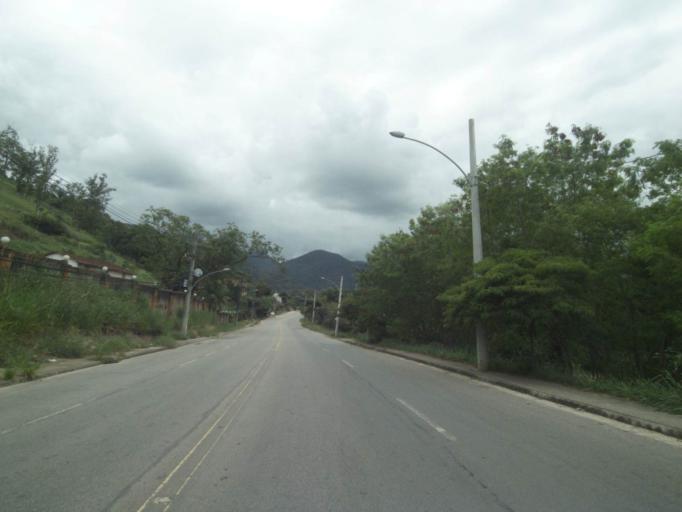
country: BR
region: Rio de Janeiro
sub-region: Nilopolis
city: Nilopolis
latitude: -22.9904
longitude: -43.5029
